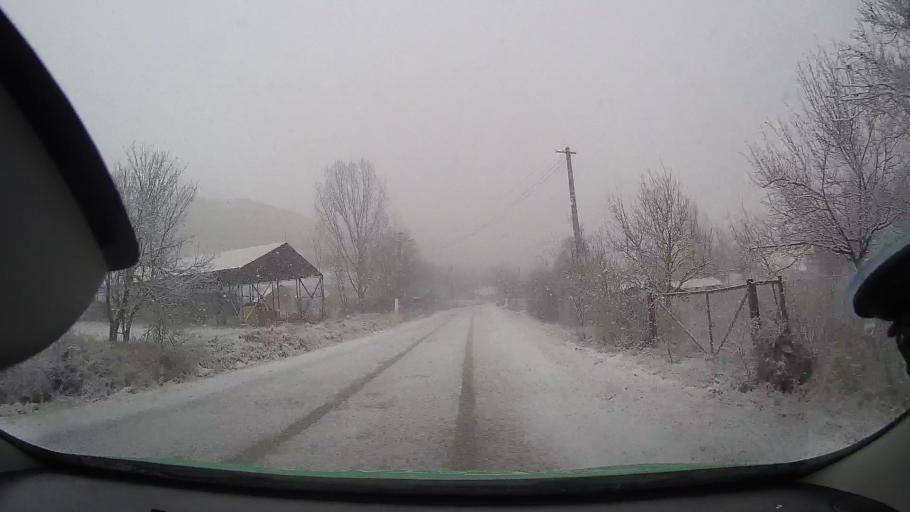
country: RO
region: Alba
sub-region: Comuna Hoparta
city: Hoparta
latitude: 46.3134
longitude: 23.8598
